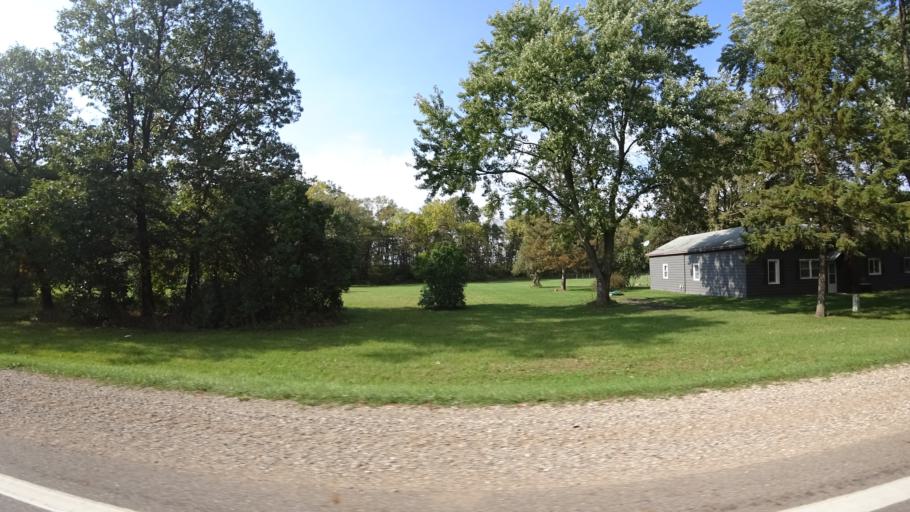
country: US
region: Michigan
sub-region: Saint Joseph County
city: Centreville
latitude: 42.0023
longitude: -85.5562
